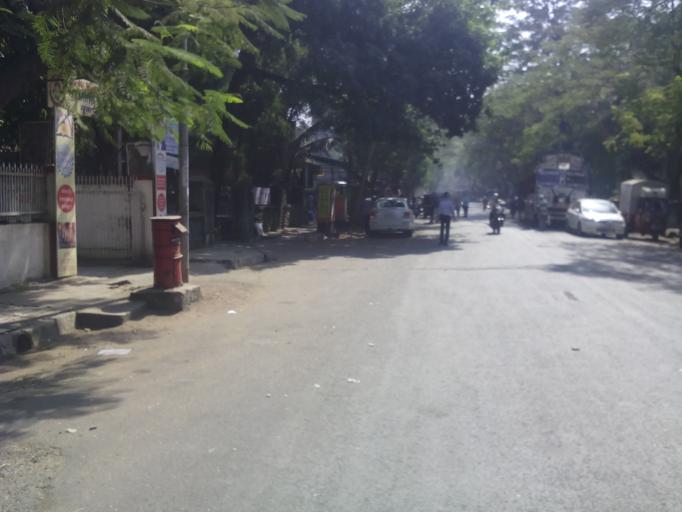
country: IN
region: Maharashtra
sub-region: Mumbai Suburban
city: Borivli
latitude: 19.2079
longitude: 72.8697
